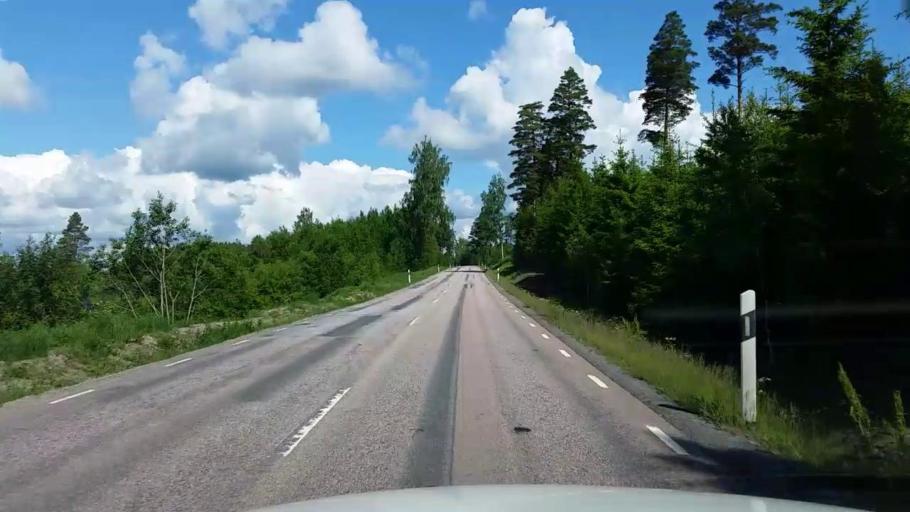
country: SE
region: Vaestmanland
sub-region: Kopings Kommun
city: Kolsva
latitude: 59.6373
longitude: 15.7968
